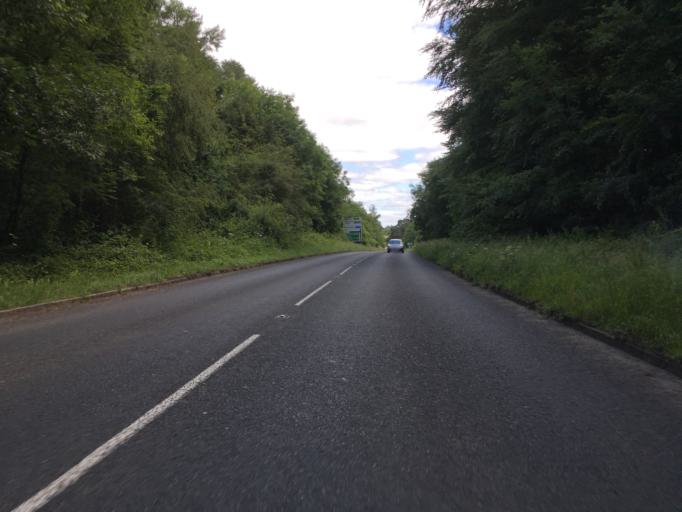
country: GB
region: England
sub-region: Hampshire
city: Highclere
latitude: 51.3603
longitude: -1.3617
